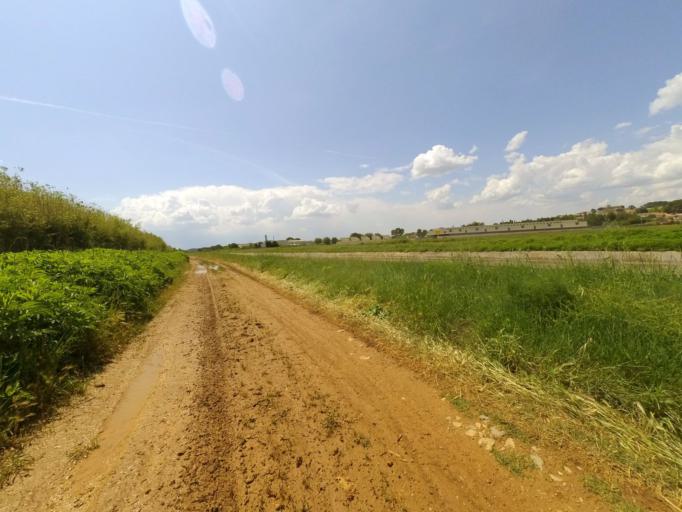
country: FR
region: Languedoc-Roussillon
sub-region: Departement du Gard
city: Gallargues-le-Montueux
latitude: 43.7164
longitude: 4.1800
